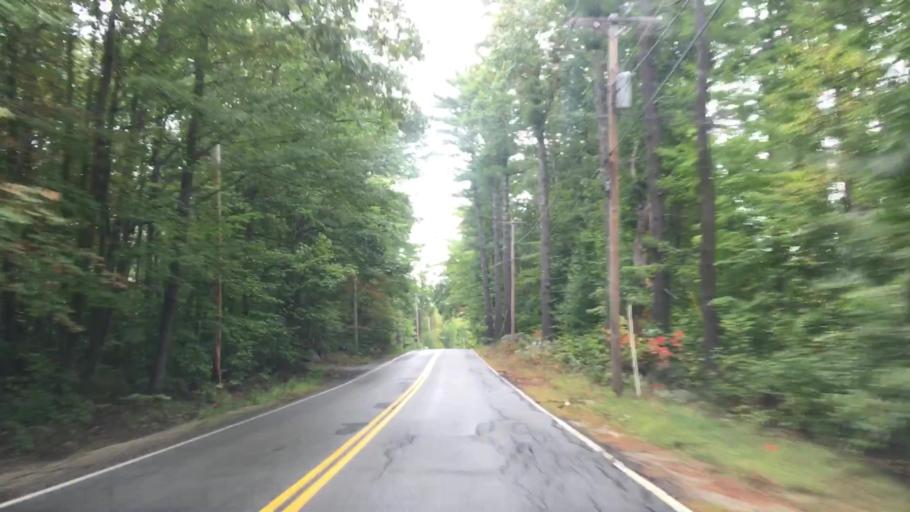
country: US
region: Maine
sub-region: Cumberland County
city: Raymond
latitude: 43.9595
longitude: -70.4649
